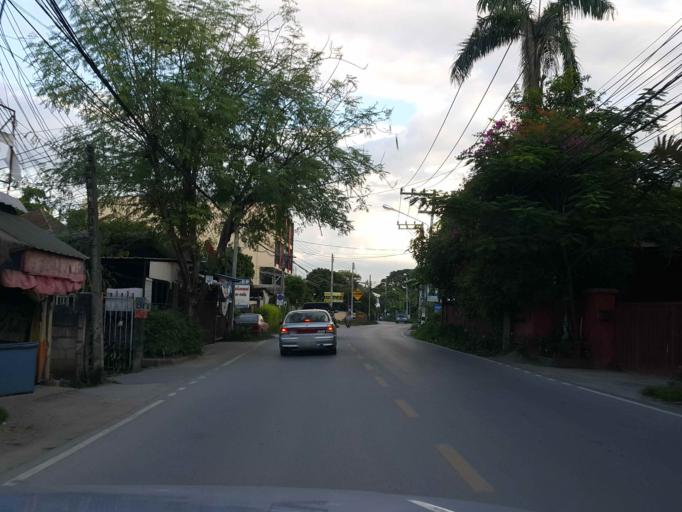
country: TH
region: Chiang Mai
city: Chiang Mai
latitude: 18.8083
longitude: 99.0049
